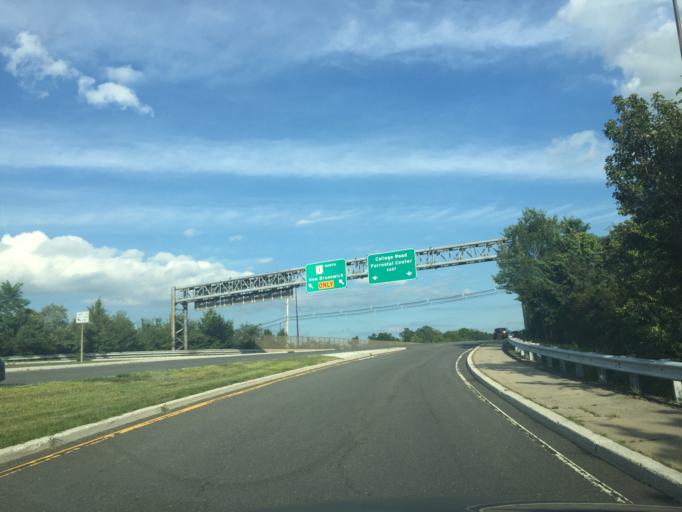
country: US
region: New Jersey
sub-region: Somerset County
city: Kingston
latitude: 40.3575
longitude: -74.6083
